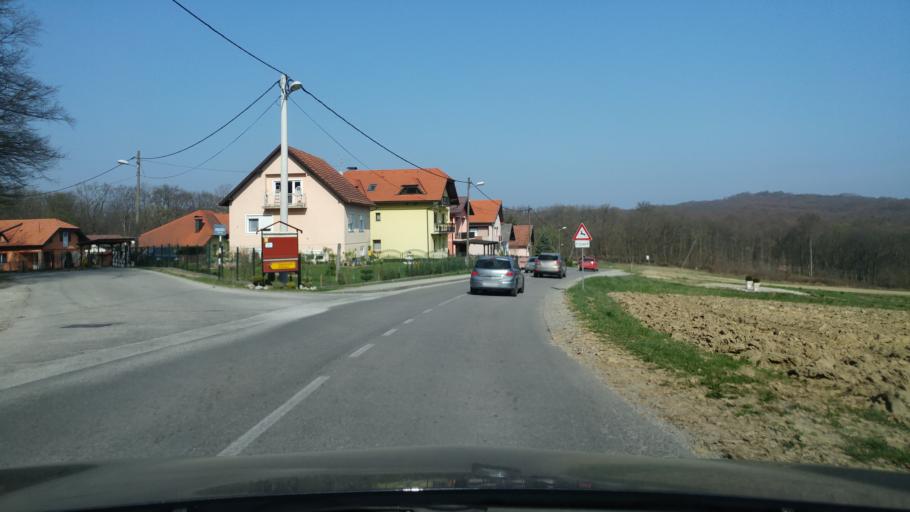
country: HR
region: Zagrebacka
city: Pojatno
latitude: 45.8931
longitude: 15.7923
